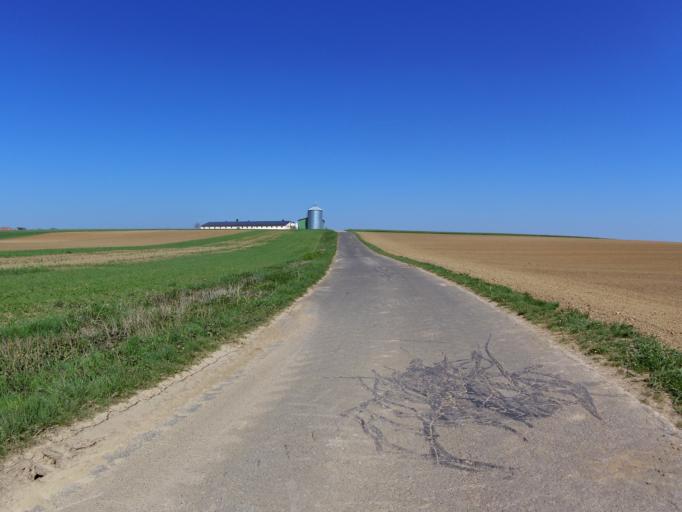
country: DE
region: Bavaria
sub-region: Regierungsbezirk Unterfranken
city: Biebelried
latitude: 49.7779
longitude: 10.0824
